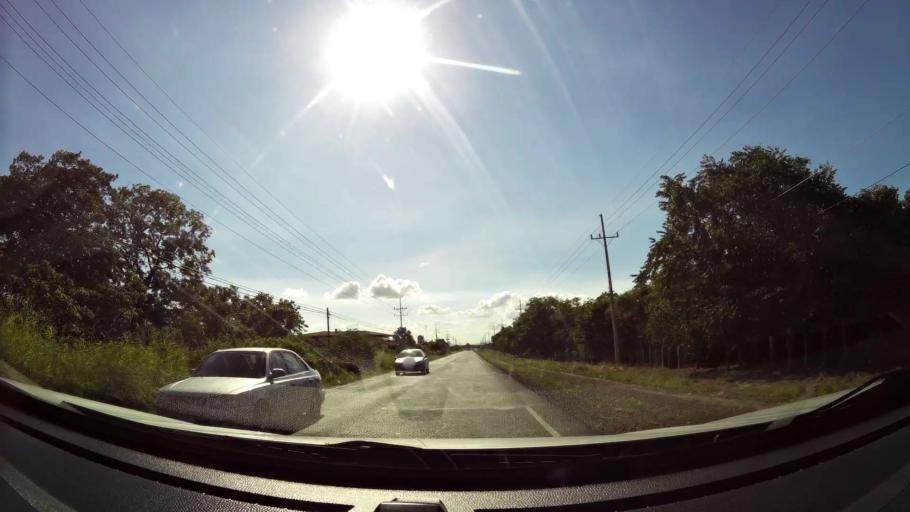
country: CR
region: Guanacaste
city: Liberia
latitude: 10.6009
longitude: -85.5182
